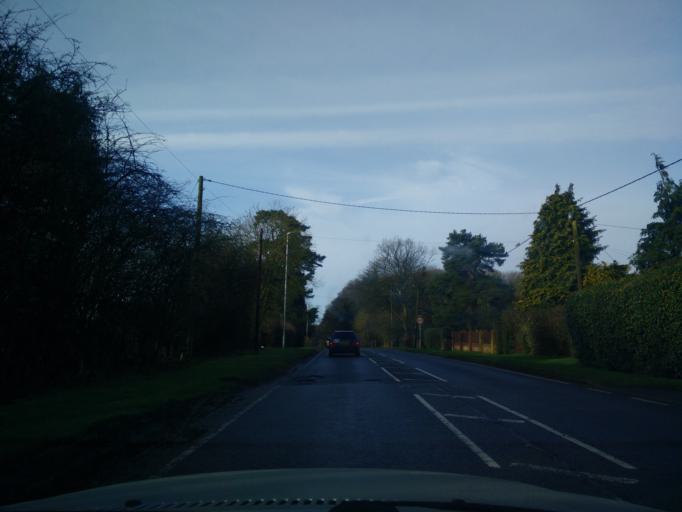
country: GB
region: England
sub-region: Buckinghamshire
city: Great Missenden
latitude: 51.6572
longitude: -0.6965
